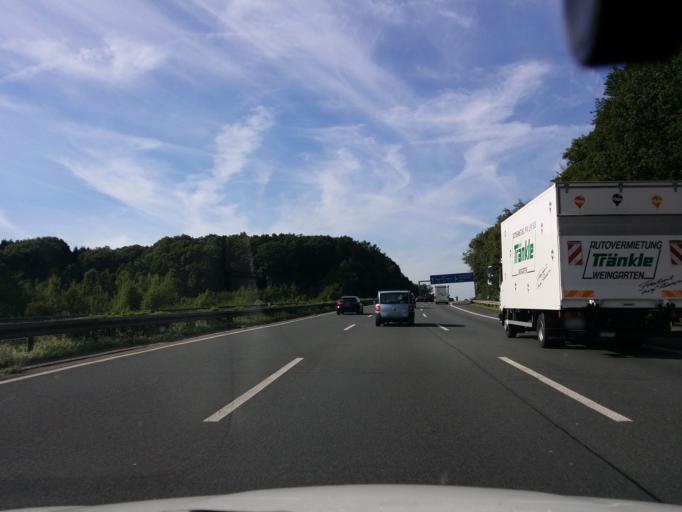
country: DE
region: North Rhine-Westphalia
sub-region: Regierungsbezirk Koln
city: Bad Honnef
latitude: 50.6804
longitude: 7.2810
